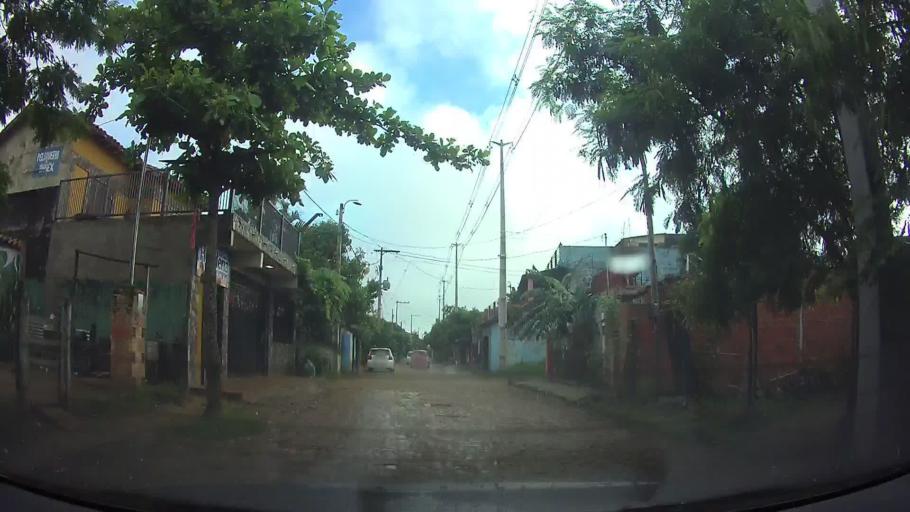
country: PY
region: Asuncion
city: Asuncion
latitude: -25.2484
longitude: -57.5832
